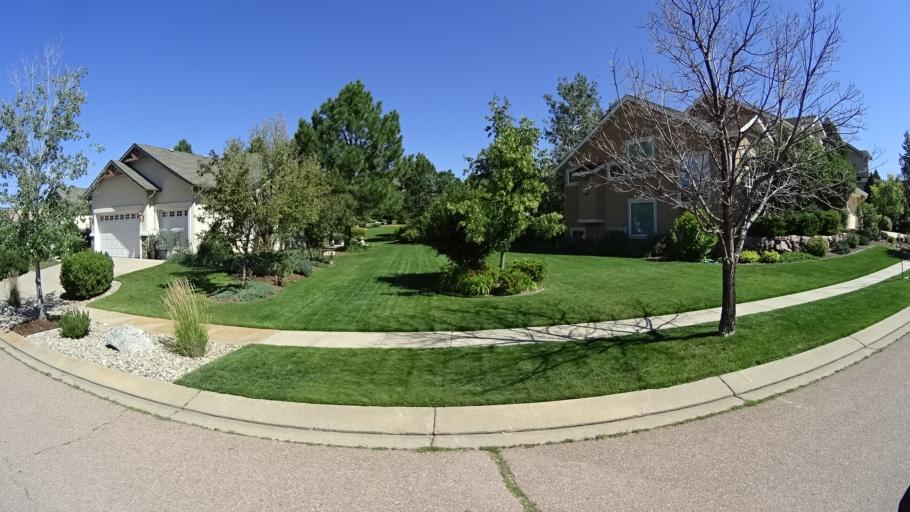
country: US
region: Colorado
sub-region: El Paso County
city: Gleneagle
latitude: 38.9712
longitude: -104.7803
